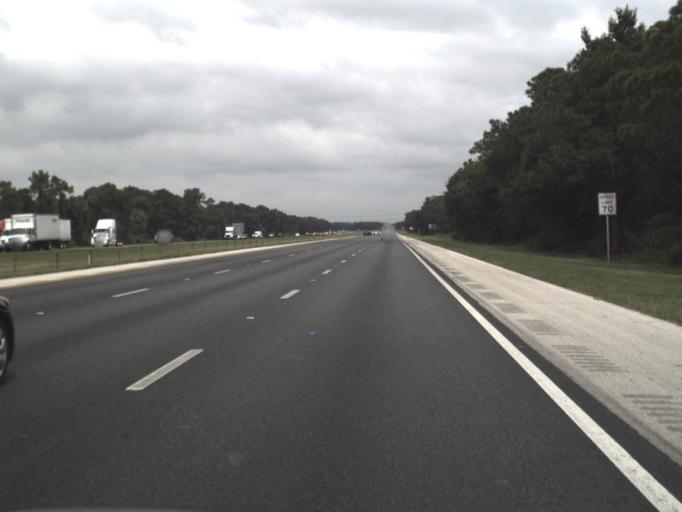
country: US
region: Florida
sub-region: Manatee County
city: Samoset
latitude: 27.4520
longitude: -82.4590
